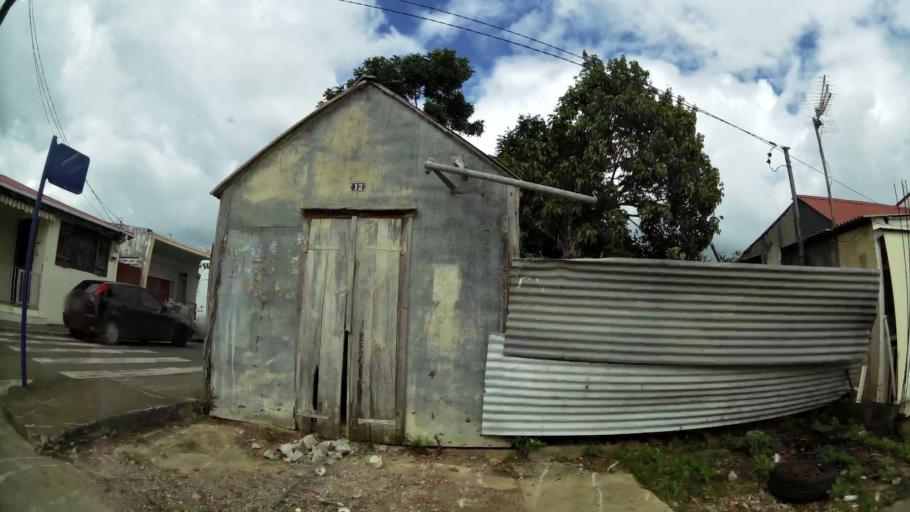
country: GP
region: Guadeloupe
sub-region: Guadeloupe
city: Baie-Mahault
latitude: 16.2665
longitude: -61.5858
